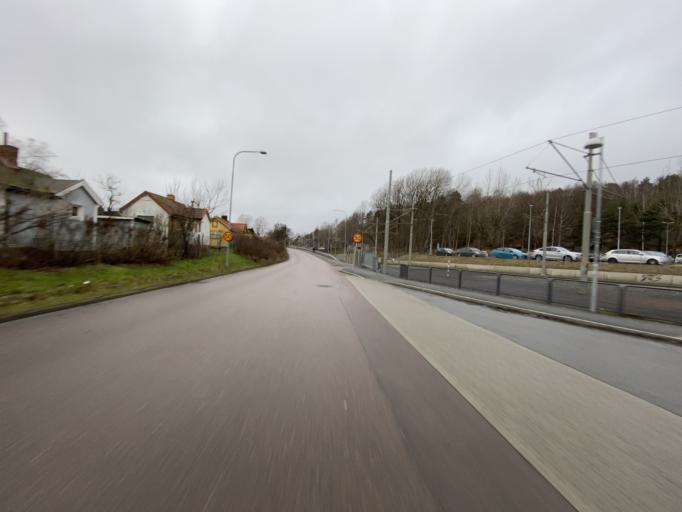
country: SE
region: Vaestra Goetaland
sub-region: Goteborg
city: Eriksbo
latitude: 57.7227
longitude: 12.0469
